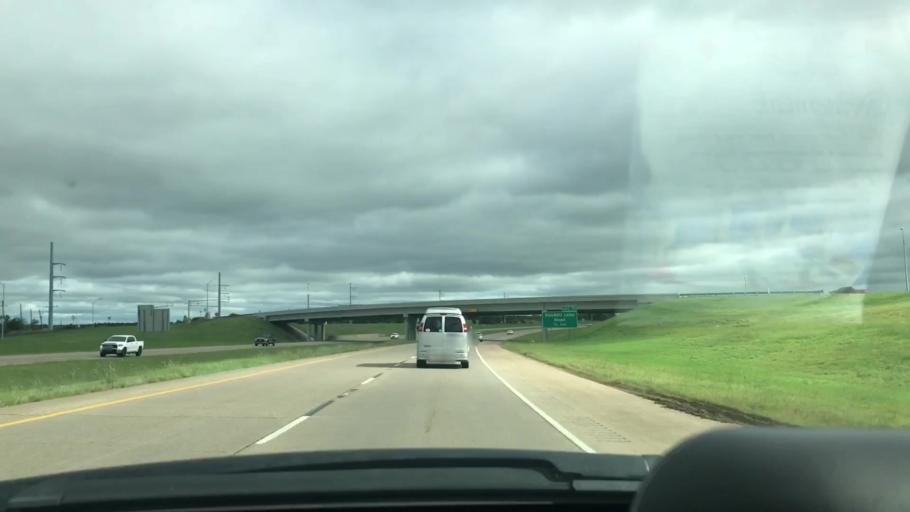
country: US
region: Texas
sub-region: Grayson County
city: Denison
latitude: 33.7767
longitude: -96.5843
